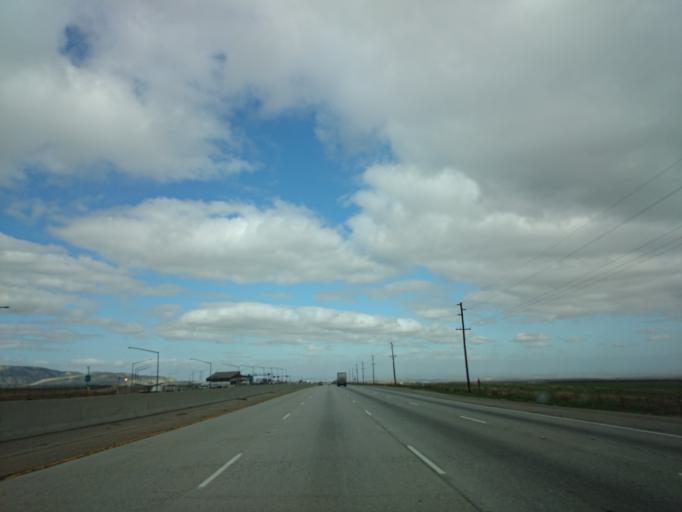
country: US
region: California
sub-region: Kern County
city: Frazier Park
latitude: 34.9568
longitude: -118.9359
